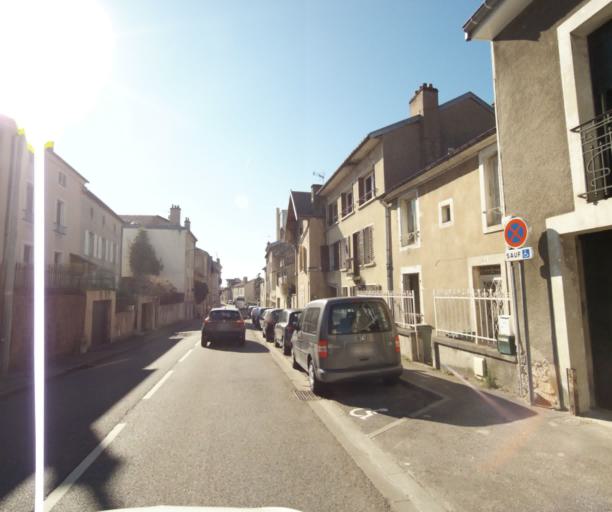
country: FR
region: Lorraine
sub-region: Departement de Meurthe-et-Moselle
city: Malzeville
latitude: 48.7126
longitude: 6.1844
